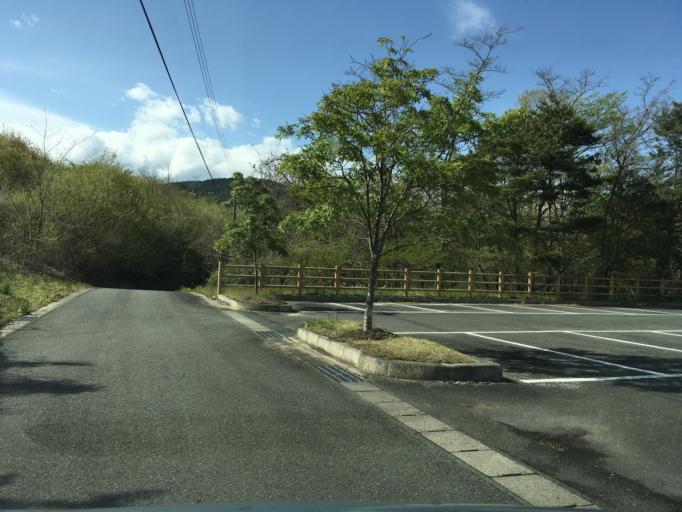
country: JP
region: Iwate
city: Ichinoseki
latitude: 38.8421
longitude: 141.3922
